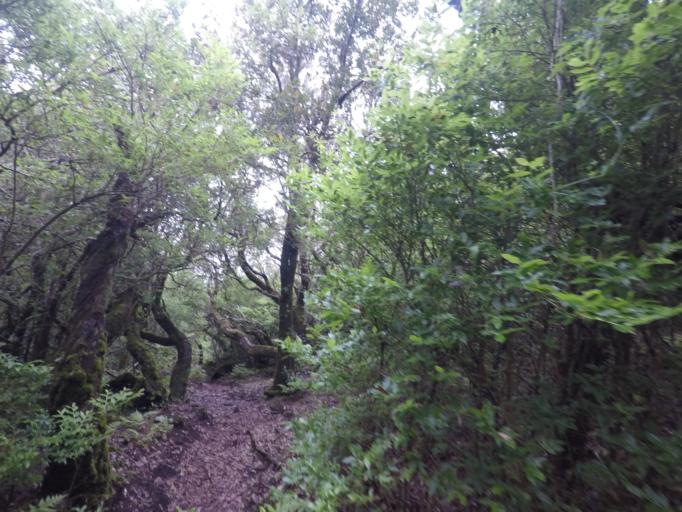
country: PT
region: Madeira
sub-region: Sao Vicente
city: Sao Vicente
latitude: 32.7692
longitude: -17.0570
